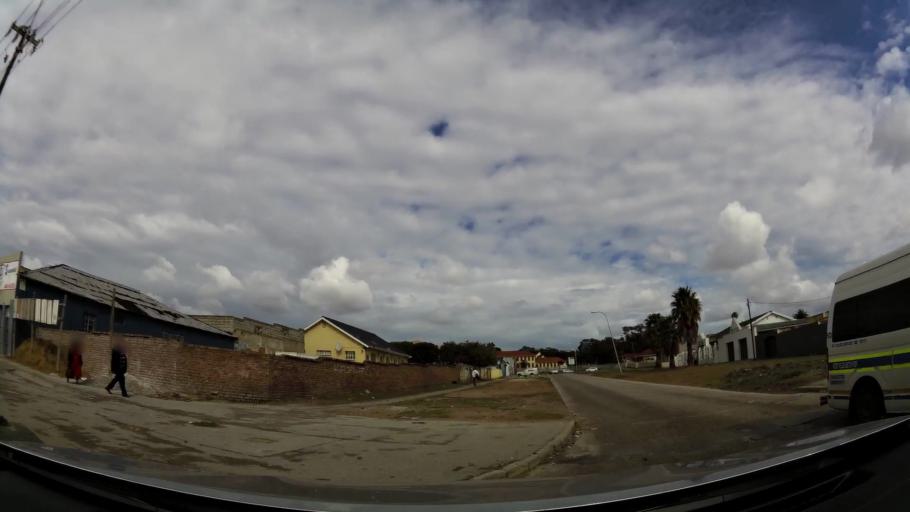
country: ZA
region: Eastern Cape
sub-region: Nelson Mandela Bay Metropolitan Municipality
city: Port Elizabeth
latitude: -33.9299
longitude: 25.5735
